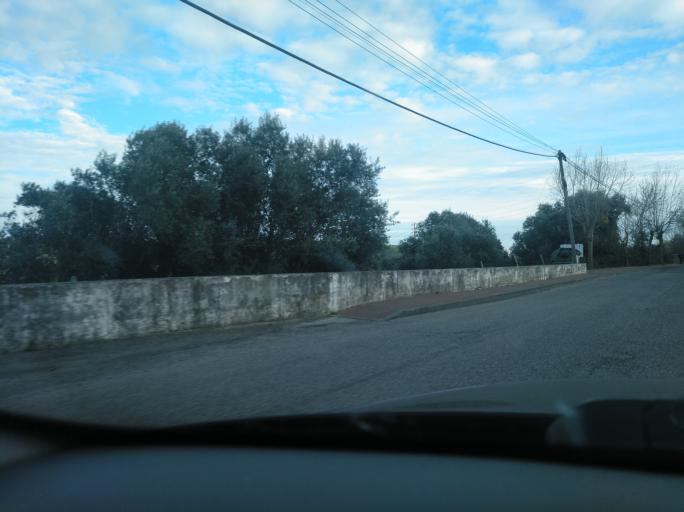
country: PT
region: Lisbon
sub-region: Loures
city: Unhos
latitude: 38.8336
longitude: -9.1254
